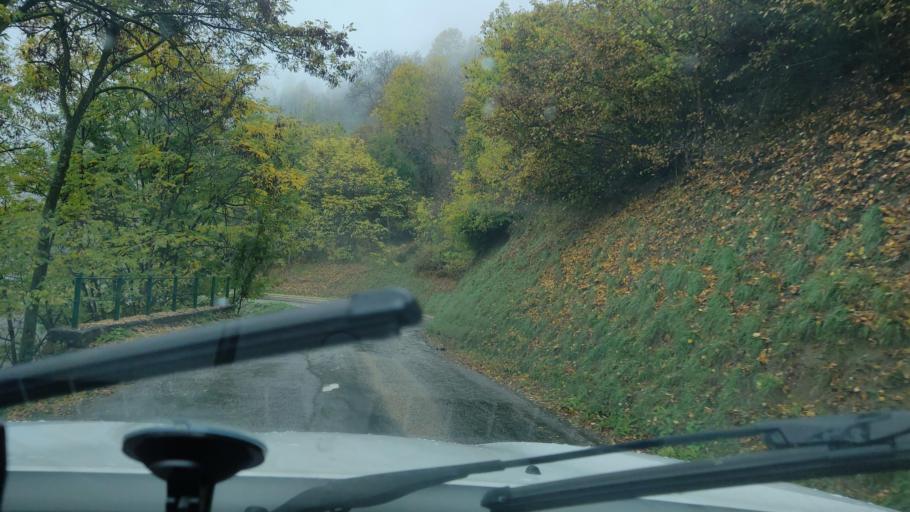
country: FR
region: Rhone-Alpes
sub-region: Departement de la Savoie
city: Les Allues
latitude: 45.4628
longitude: 6.5714
